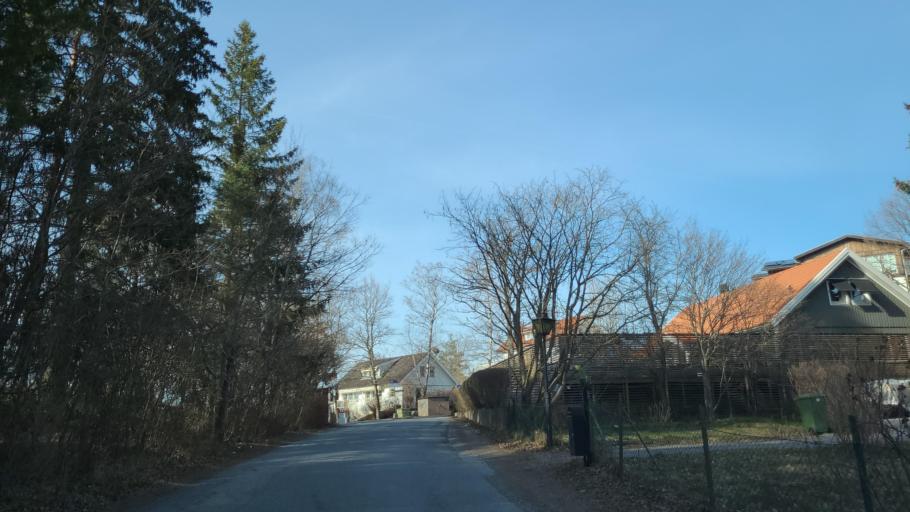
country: SE
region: Stockholm
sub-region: Ekero Kommun
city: Ekeroe
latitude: 59.2853
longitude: 17.7706
